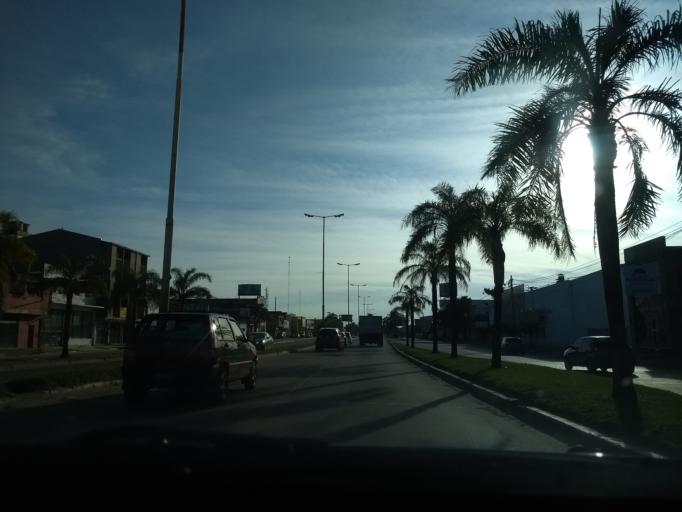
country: AR
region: Corrientes
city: Corrientes
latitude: -27.4835
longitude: -58.7916
